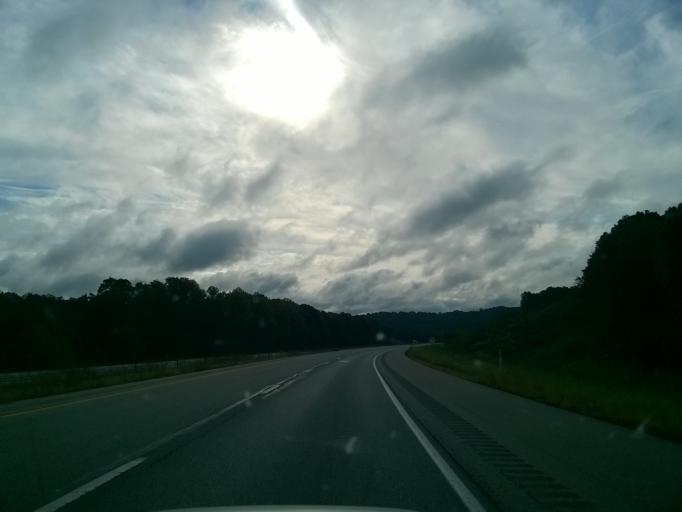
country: US
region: Indiana
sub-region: Crawford County
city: English
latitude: 38.2290
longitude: -86.6470
